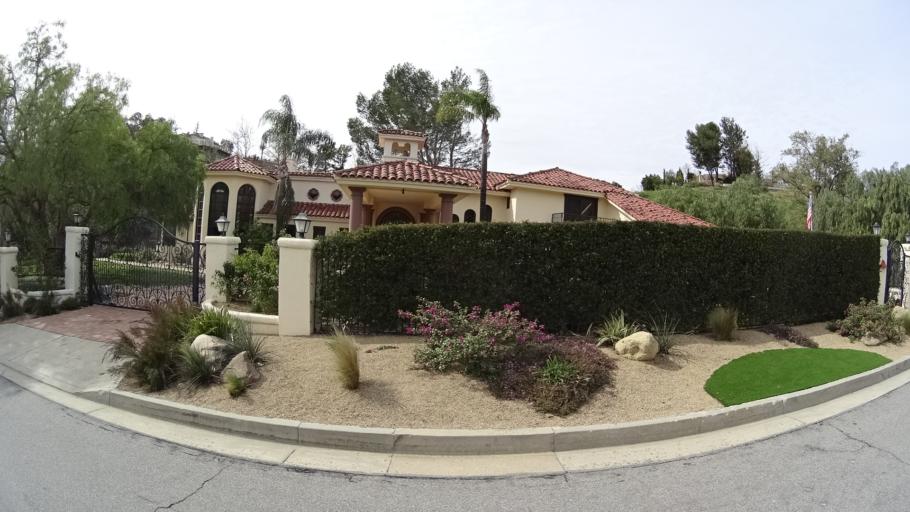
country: US
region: California
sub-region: Orange County
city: Villa Park
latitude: 33.8319
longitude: -117.7447
